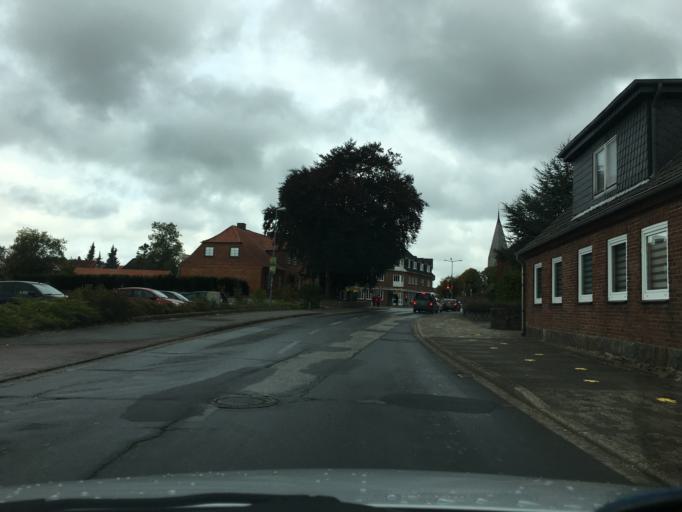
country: DE
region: Schleswig-Holstein
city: Gettorf
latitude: 54.4061
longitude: 9.9744
